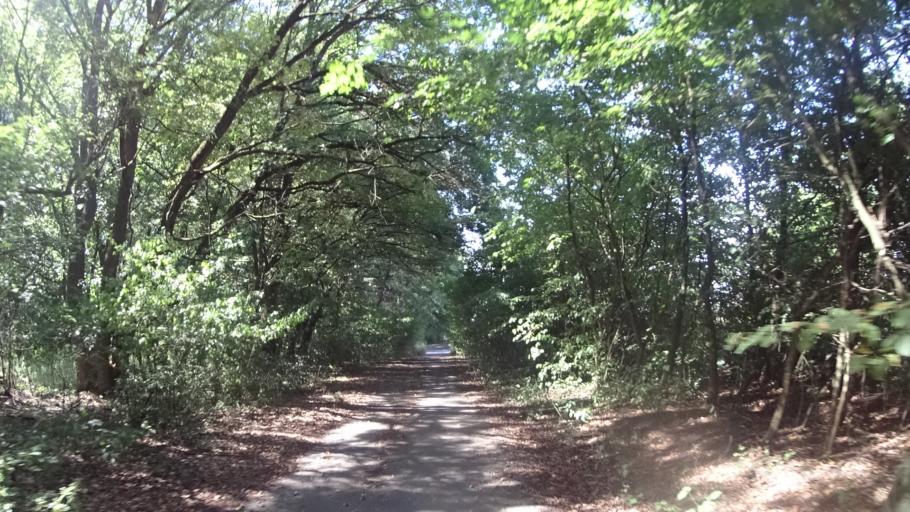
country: AT
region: Lower Austria
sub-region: Politischer Bezirk Ganserndorf
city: Angern an der March
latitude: 48.3532
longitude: 16.8862
